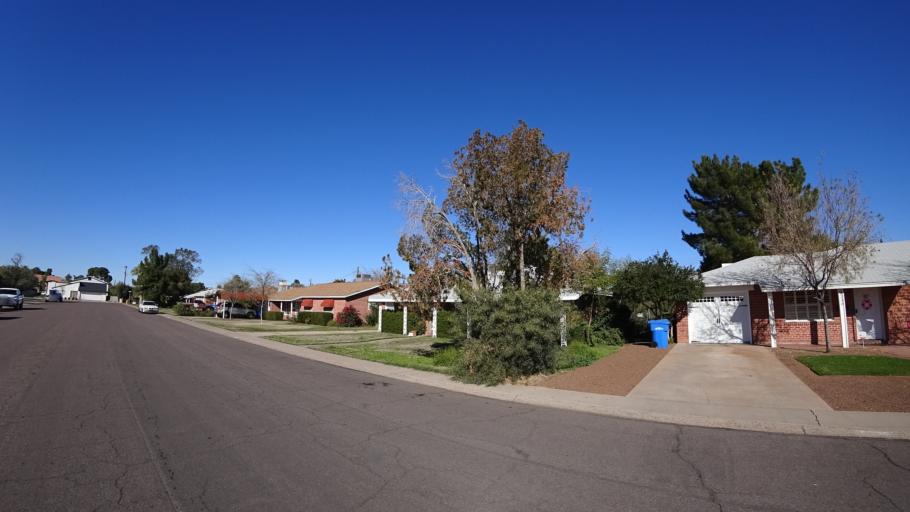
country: US
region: Arizona
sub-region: Maricopa County
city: Phoenix
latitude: 33.4966
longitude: -112.0333
